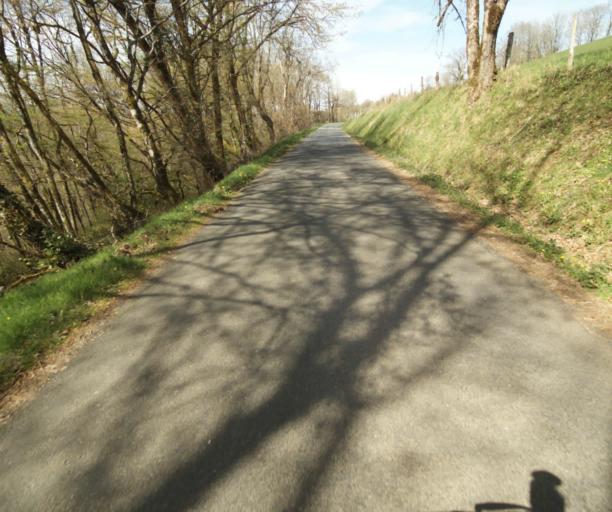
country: FR
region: Limousin
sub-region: Departement de la Correze
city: Naves
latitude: 45.3499
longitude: 1.7779
